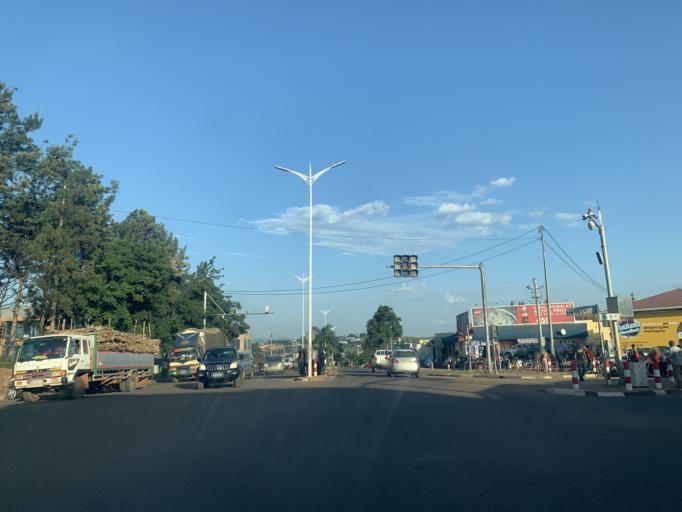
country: RW
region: Kigali
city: Kigali
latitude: -1.9609
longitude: 30.1202
